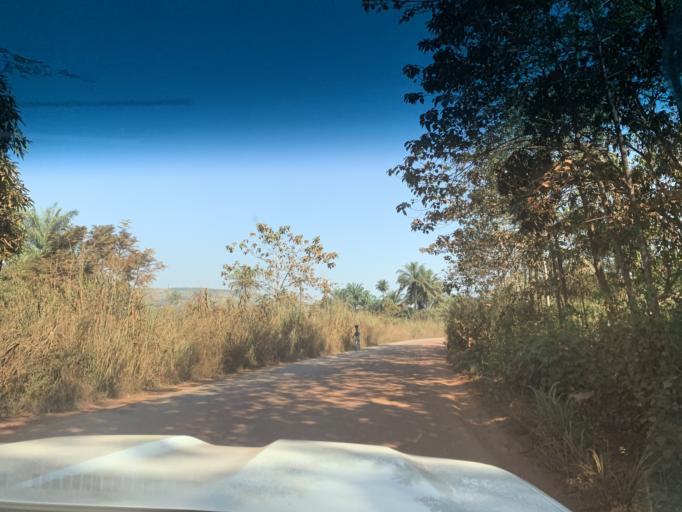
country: GN
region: Kindia
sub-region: Kindia
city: Kindia
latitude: 9.9197
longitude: -12.9969
